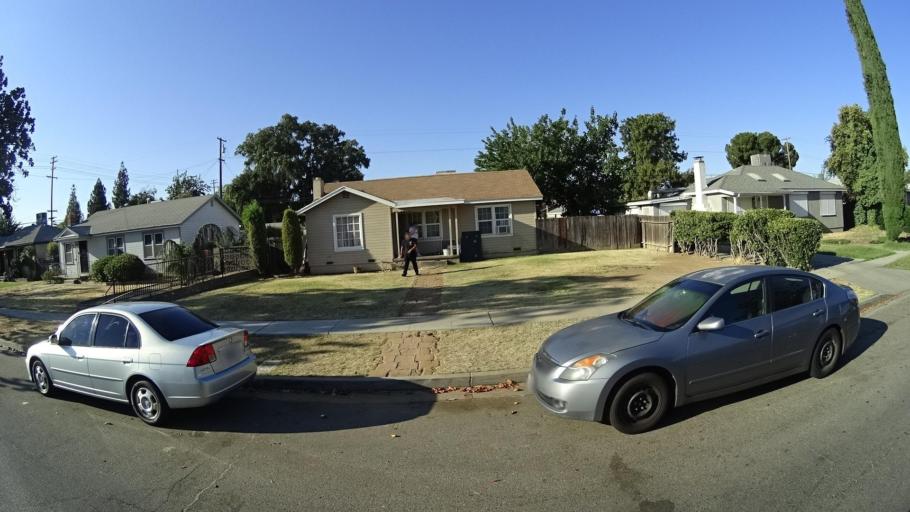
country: US
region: California
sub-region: Fresno County
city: Fresno
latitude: 36.7738
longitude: -119.8276
